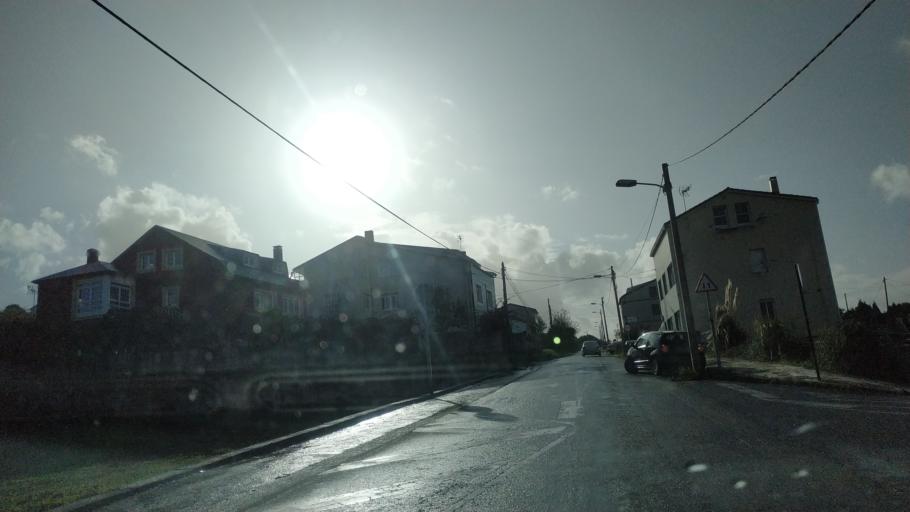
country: ES
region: Galicia
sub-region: Provincia da Coruna
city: A Coruna
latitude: 43.3331
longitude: -8.4061
